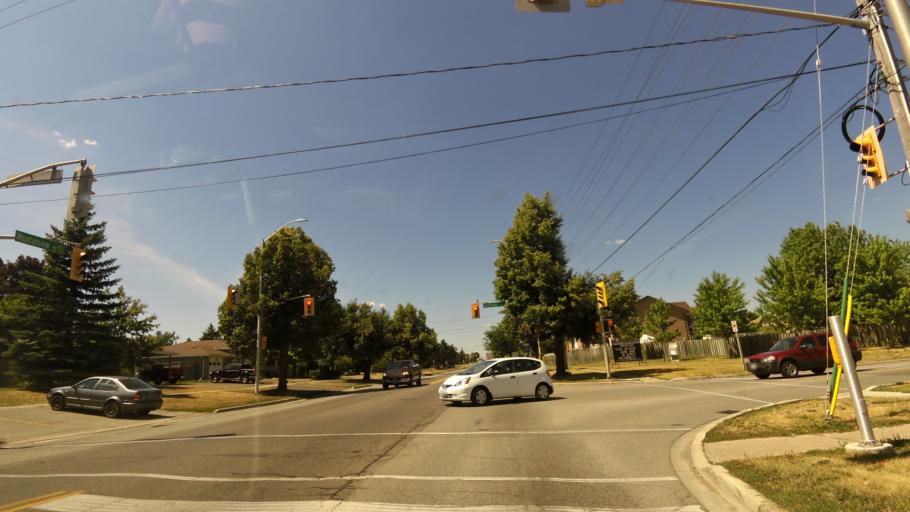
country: CA
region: Ontario
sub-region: Halton
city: Milton
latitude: 43.6457
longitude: -79.8972
